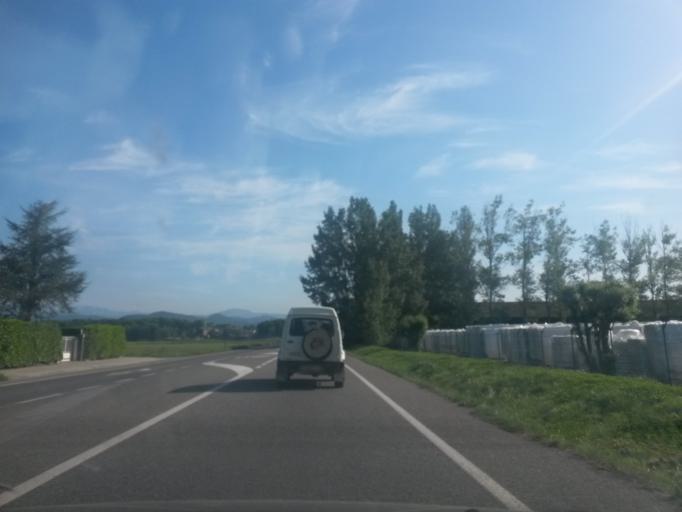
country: ES
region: Catalonia
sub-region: Provincia de Girona
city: Bas
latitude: 42.1518
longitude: 2.4628
